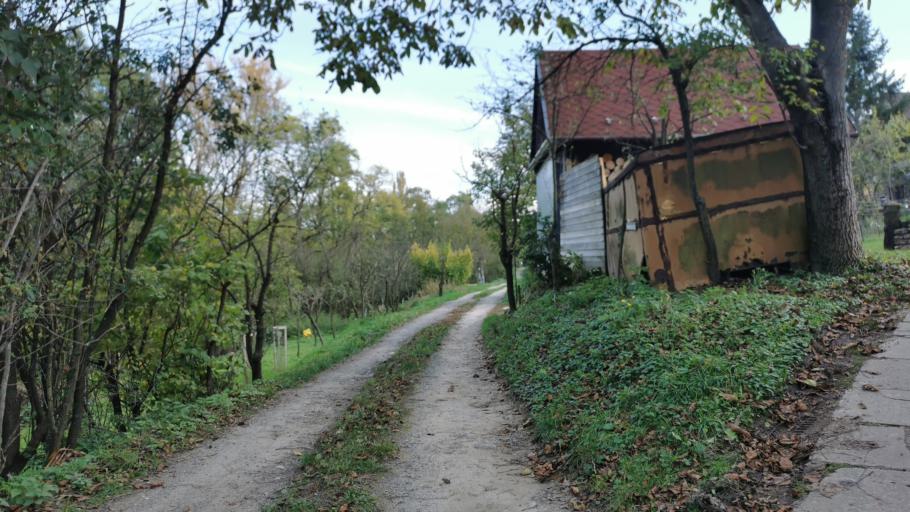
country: SK
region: Trnavsky
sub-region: Okres Skalica
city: Skalica
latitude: 48.8216
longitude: 17.2315
